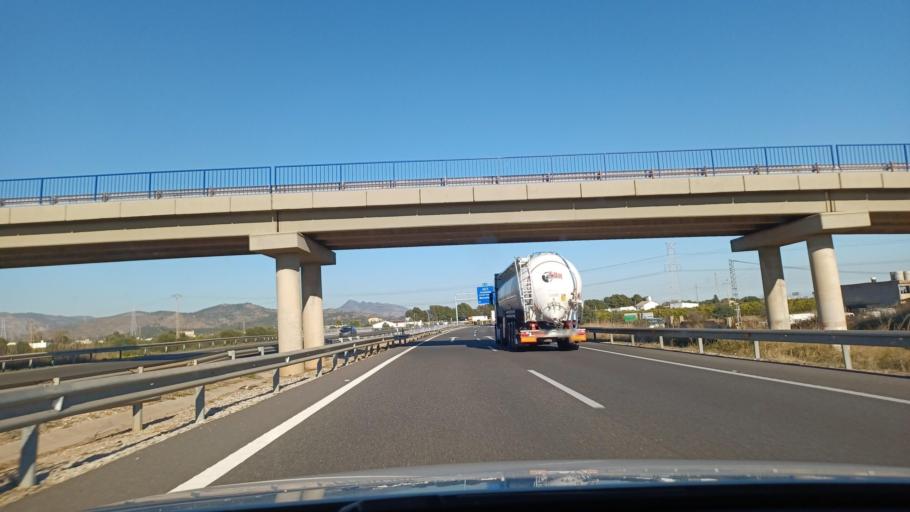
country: ES
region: Valencia
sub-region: Provincia de Castello
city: Vila-real
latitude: 39.9807
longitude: -0.1027
